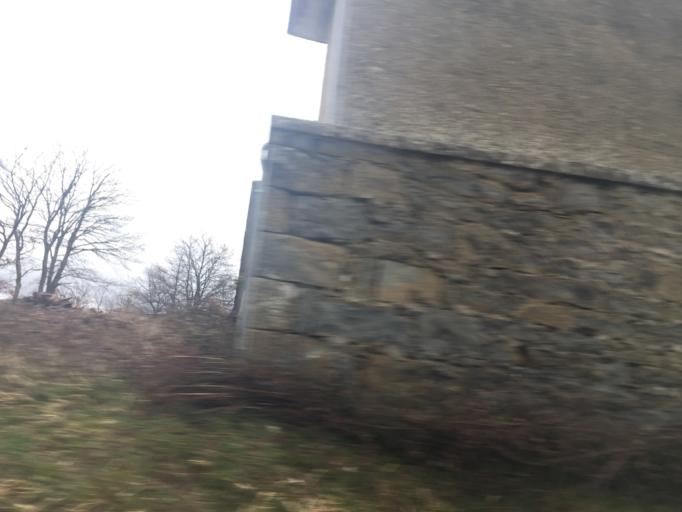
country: IT
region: The Marches
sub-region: Provincia di Ascoli Piceno
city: Arquata del Tronto
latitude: 42.7571
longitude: 13.2950
